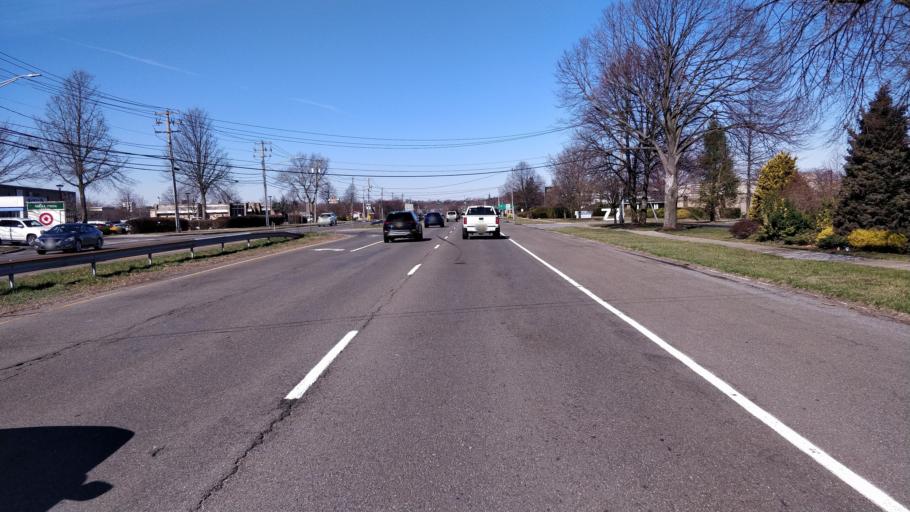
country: US
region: New York
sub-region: Suffolk County
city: Commack
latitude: 40.8409
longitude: -73.2848
